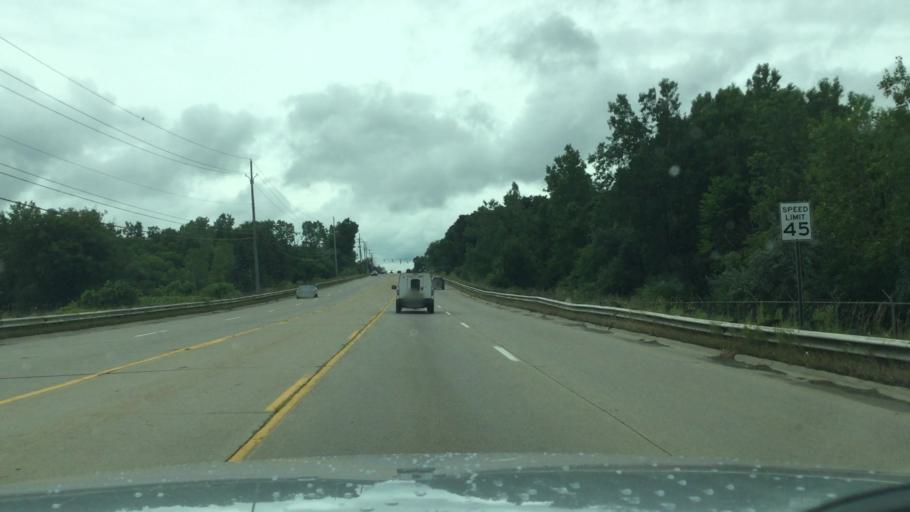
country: US
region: Michigan
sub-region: Genesee County
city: Flushing
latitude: 43.0356
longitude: -83.7736
